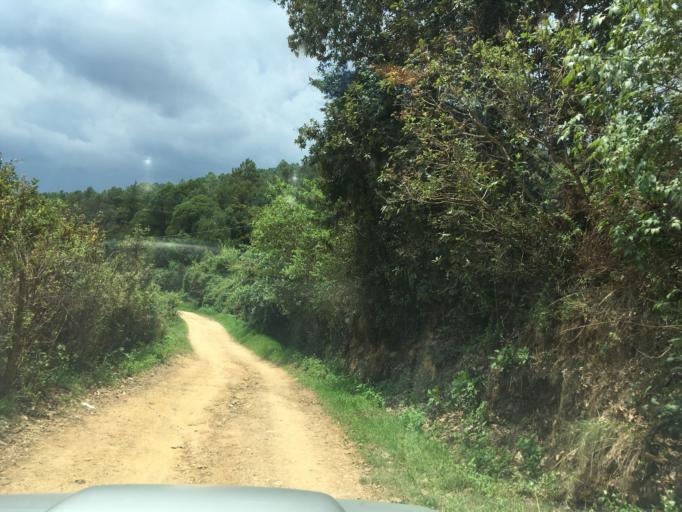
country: MX
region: Michoacan
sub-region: Zitacuaro
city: Macutzio
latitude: 19.4984
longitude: -100.3301
